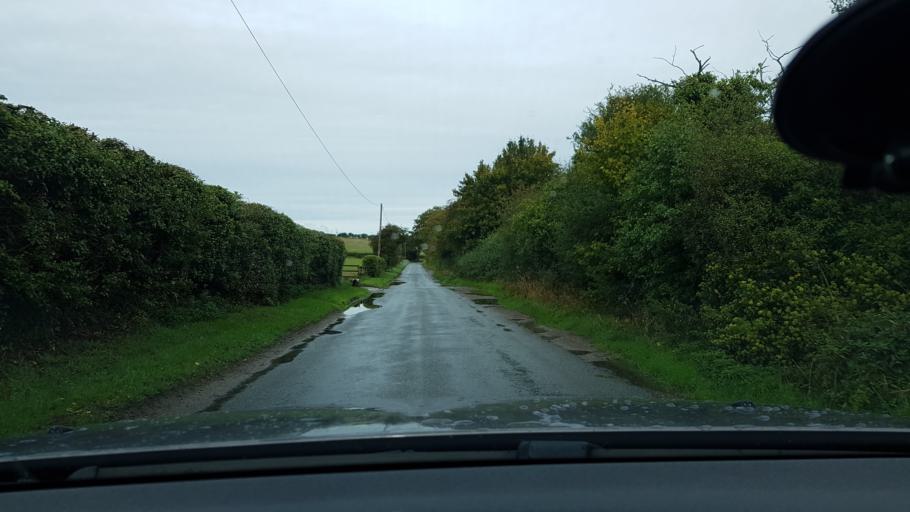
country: GB
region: England
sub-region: West Berkshire
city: Lambourn
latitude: 51.5356
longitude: -1.5284
